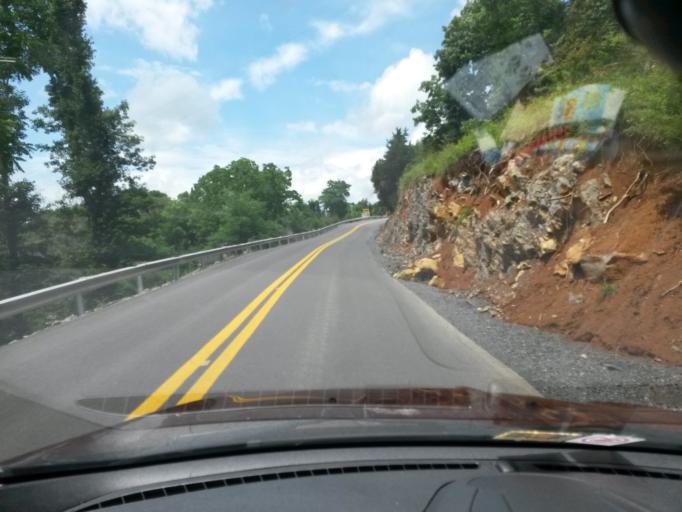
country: US
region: West Virginia
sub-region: Monroe County
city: Union
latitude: 37.5374
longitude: -80.5383
